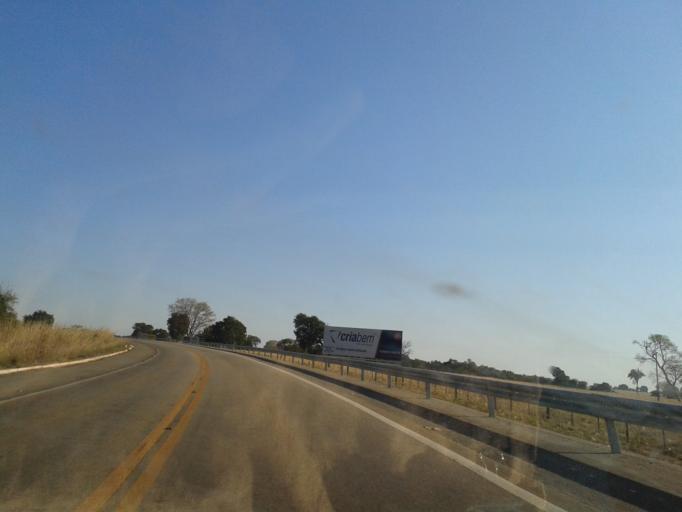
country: BR
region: Goias
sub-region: Mozarlandia
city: Mozarlandia
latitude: -15.1089
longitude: -50.6077
